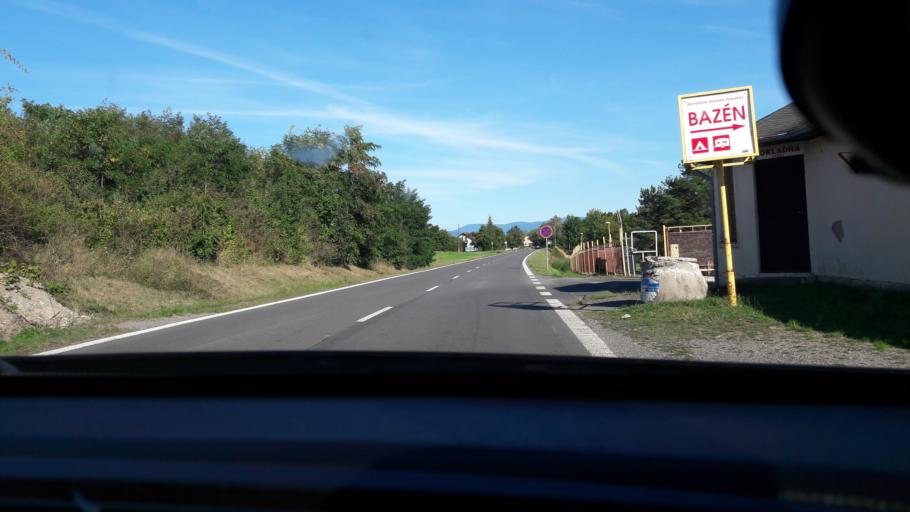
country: SK
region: Kosicky
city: Vinne
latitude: 48.8101
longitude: 22.0202
